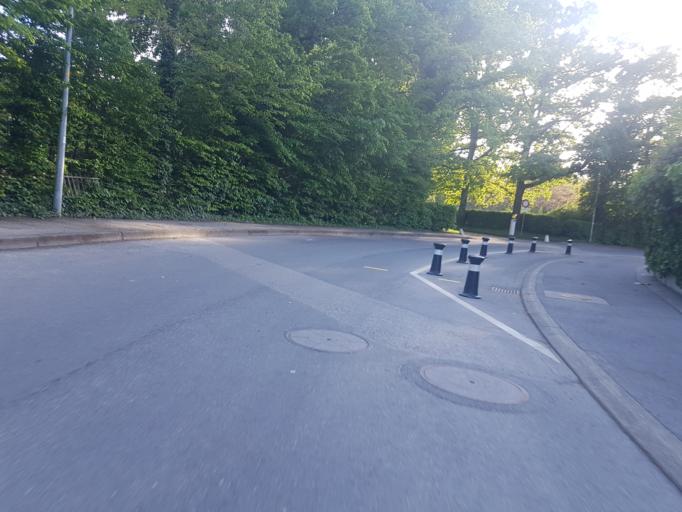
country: CH
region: Geneva
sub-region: Geneva
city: Vernier
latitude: 46.2141
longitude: 6.0888
